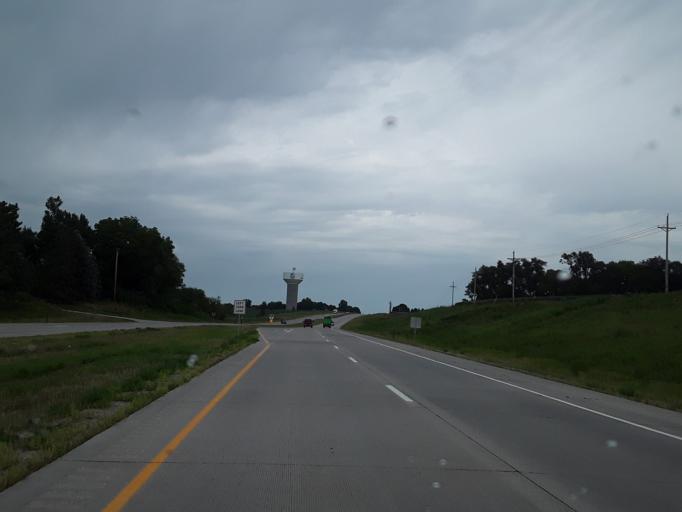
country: US
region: Nebraska
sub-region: Washington County
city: Blair
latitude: 41.4931
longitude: -96.1483
